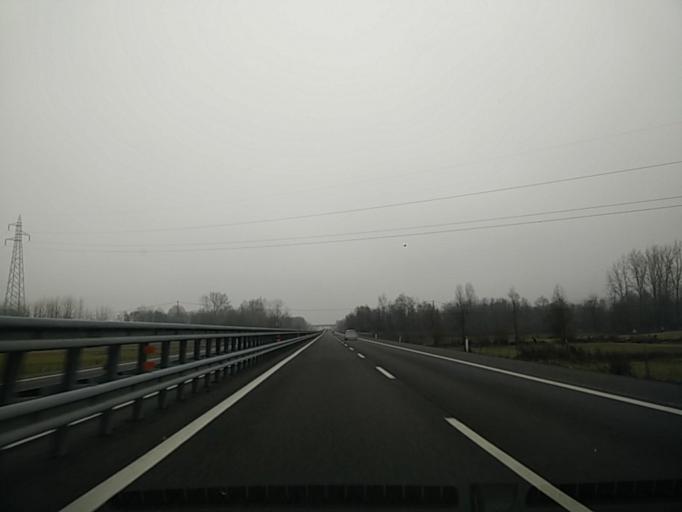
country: IT
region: Piedmont
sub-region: Provincia di Asti
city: Villafranca d'Asti
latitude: 44.9271
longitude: 8.0110
